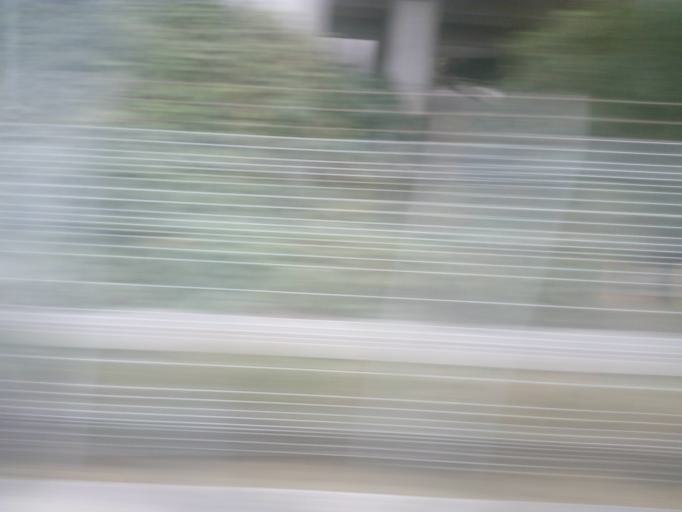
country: HK
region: Tsuen Wan
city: Tsuen Wan
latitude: 22.3359
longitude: 114.0335
